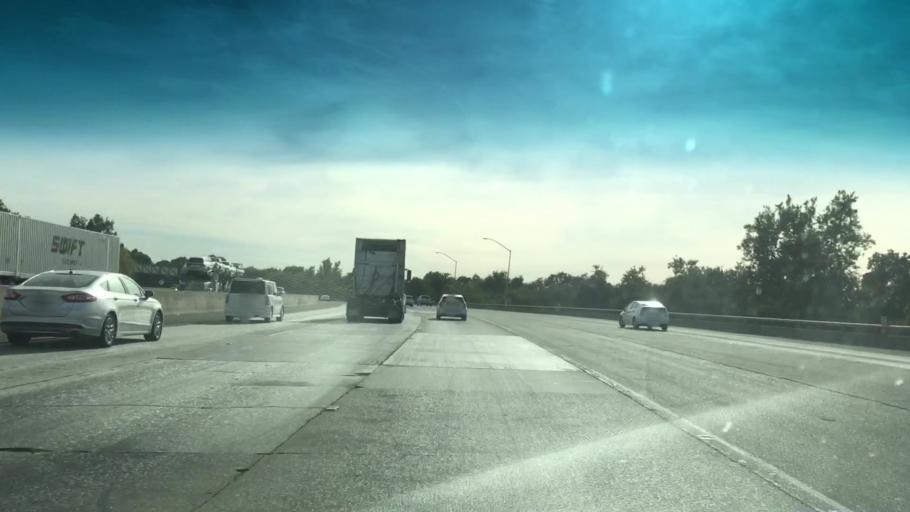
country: US
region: California
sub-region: Yolo County
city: West Sacramento
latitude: 38.5660
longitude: -121.5137
